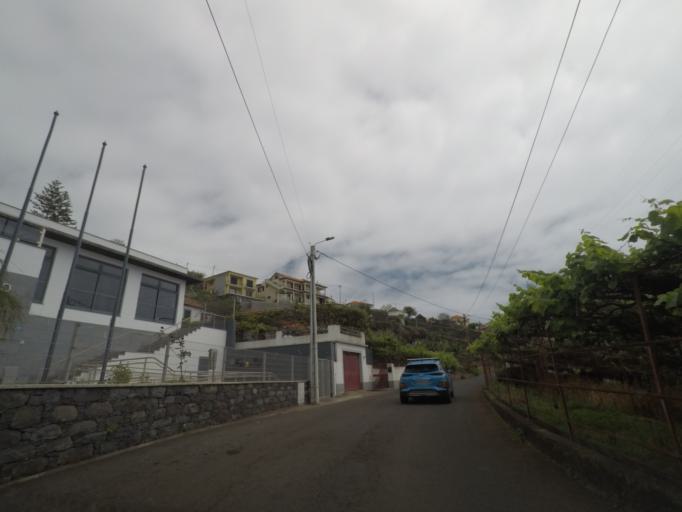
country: PT
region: Madeira
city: Ponta do Sol
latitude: 32.6918
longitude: -17.0981
